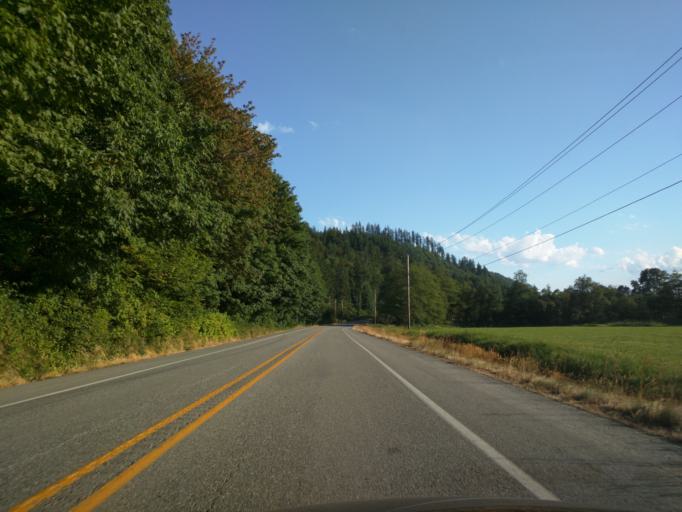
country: US
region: Washington
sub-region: Snohomish County
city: Arlington Heights
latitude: 48.2614
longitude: -122.0236
